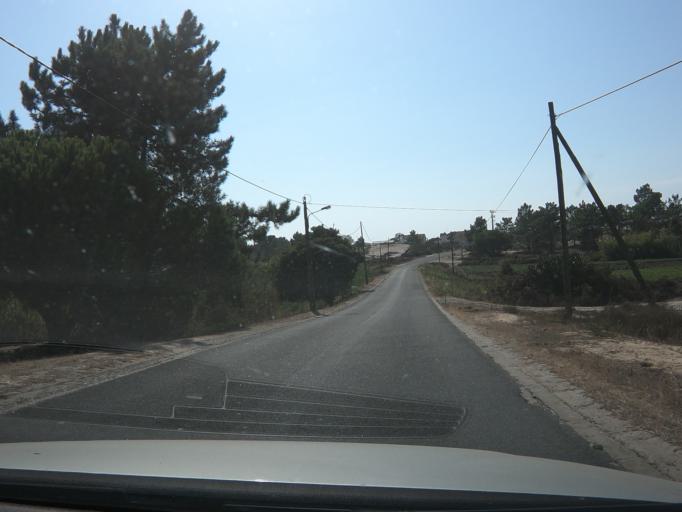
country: PT
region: Setubal
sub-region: Setubal
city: Setubal
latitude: 38.3985
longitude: -8.7680
